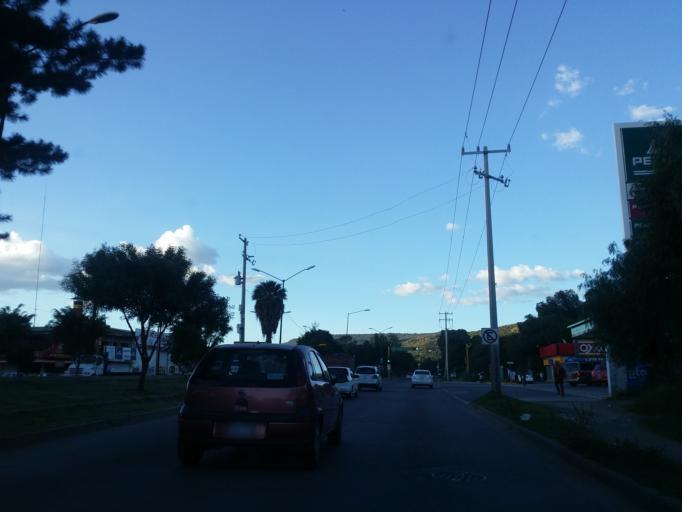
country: MX
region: Guanajuato
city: Leon
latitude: 21.1810
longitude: -101.6640
